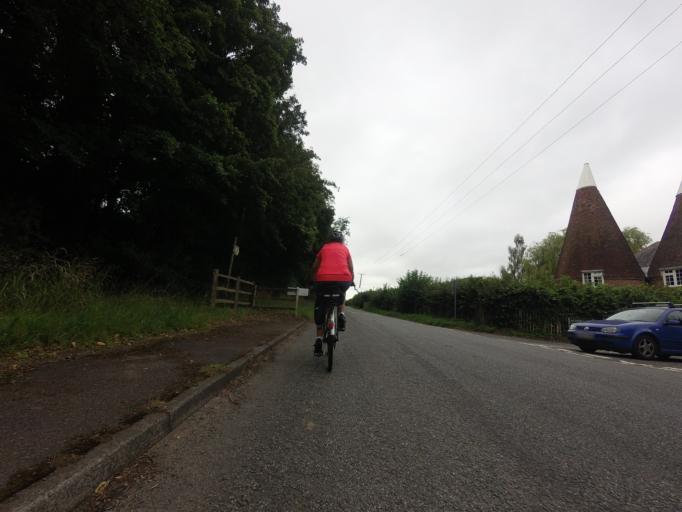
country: GB
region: England
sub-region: Kent
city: Kings Hill
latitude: 51.2931
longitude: 0.3659
